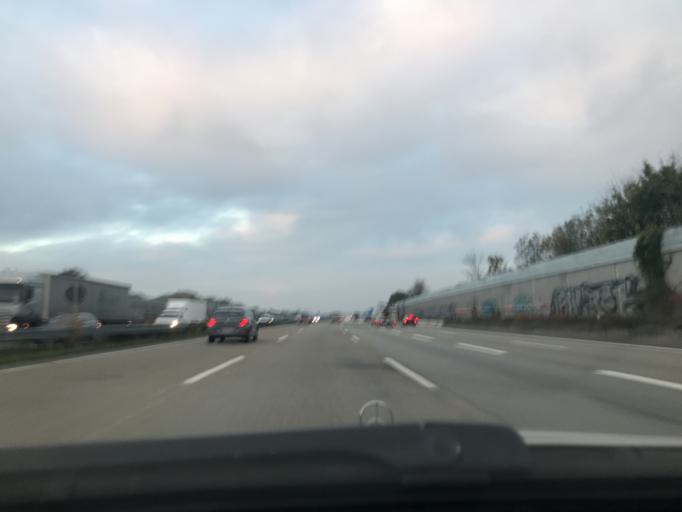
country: DE
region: North Rhine-Westphalia
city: Waltrop
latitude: 51.5835
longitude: 7.3996
